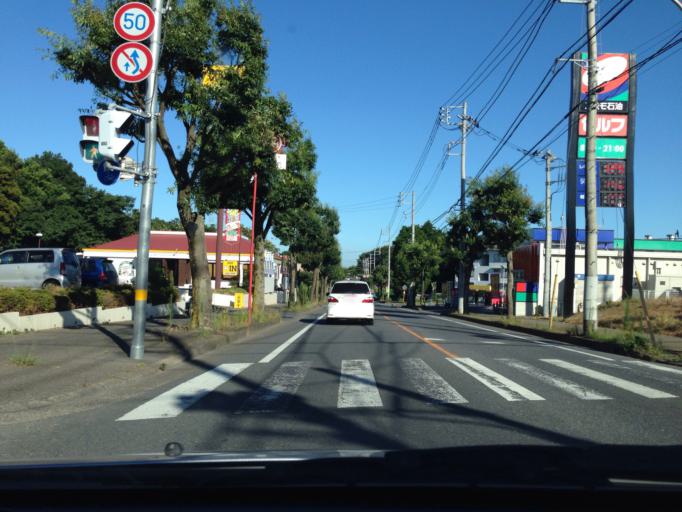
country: JP
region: Ibaraki
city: Naka
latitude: 36.0644
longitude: 140.1911
